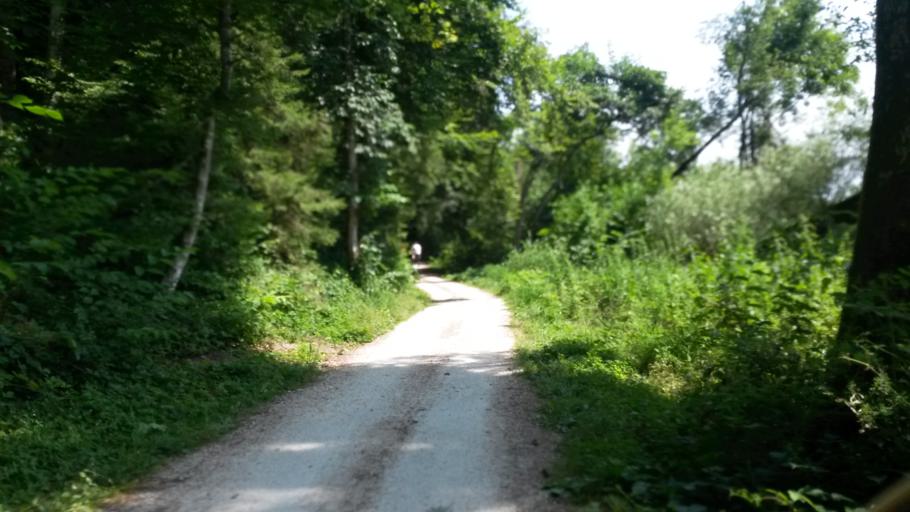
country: DE
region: Bavaria
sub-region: Upper Bavaria
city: Gstadt am Chiemsee
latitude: 47.9059
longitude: 12.4321
